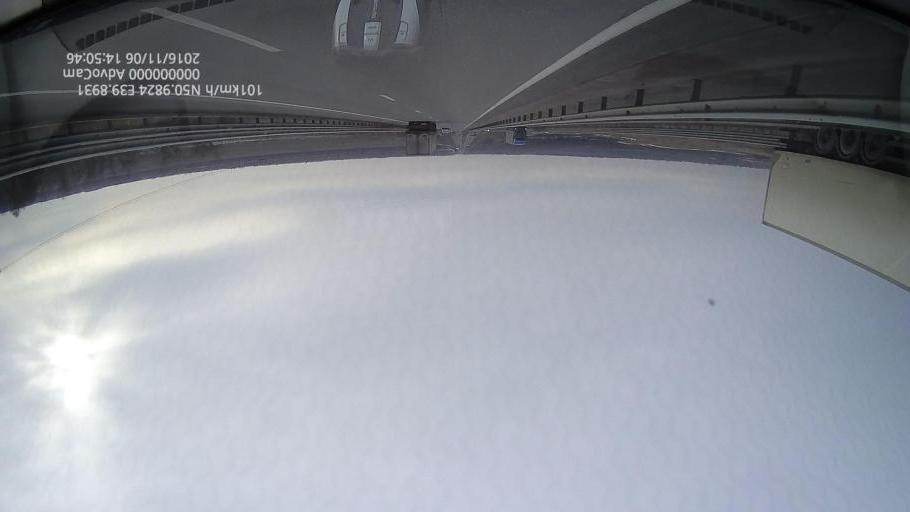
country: RU
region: Voronezj
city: Sredniy Ikorets
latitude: 50.9657
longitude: 39.9050
